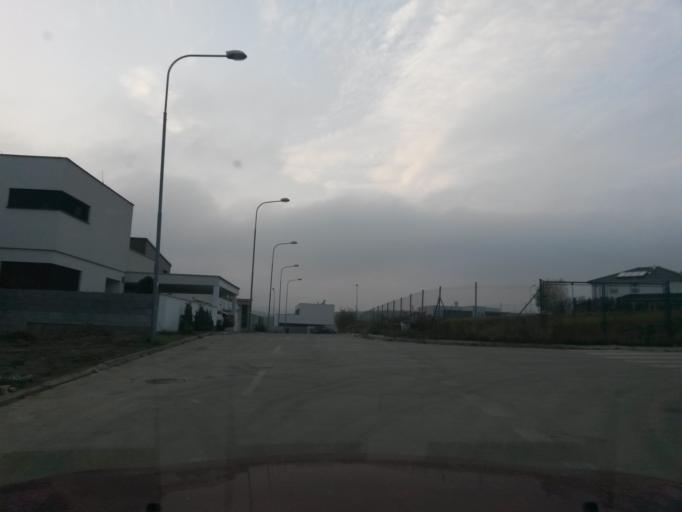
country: SK
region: Kosicky
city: Kosice
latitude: 48.7169
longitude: 21.2013
